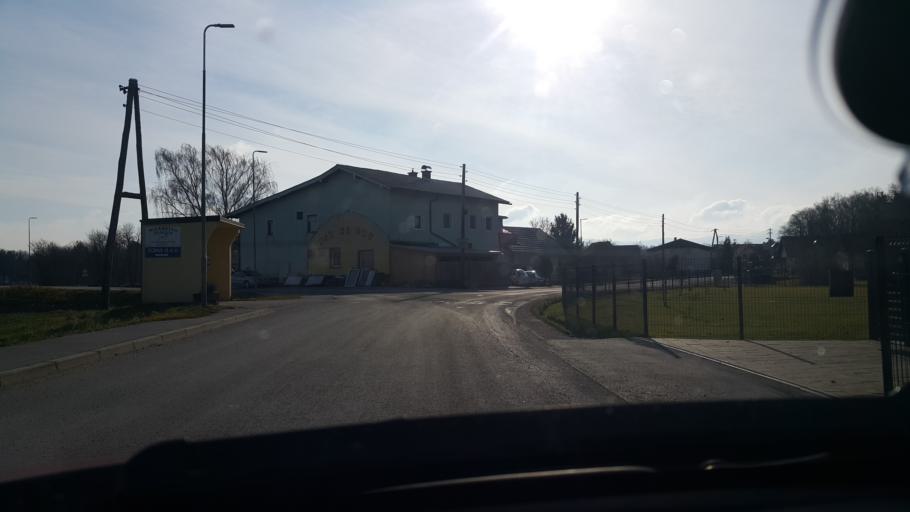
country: SI
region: Slovenska Bistrica
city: Pragersko
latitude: 46.3883
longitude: 15.6304
